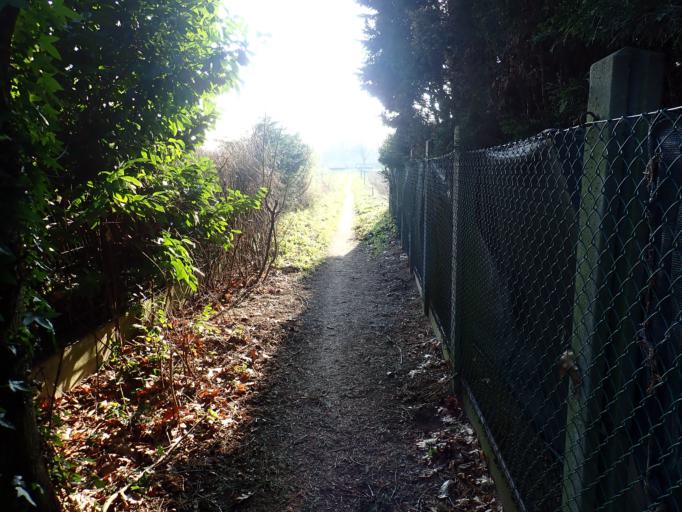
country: BE
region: Flanders
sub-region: Provincie Antwerpen
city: Borsbeek
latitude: 51.2101
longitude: 4.4956
